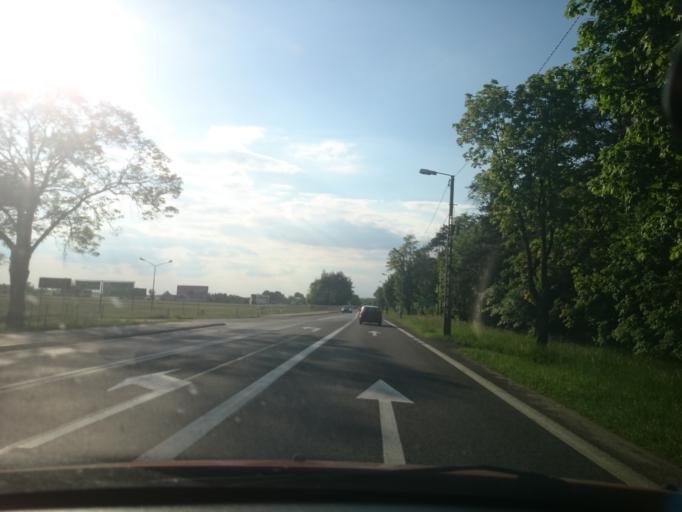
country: PL
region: Opole Voivodeship
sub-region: Powiat strzelecki
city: Izbicko
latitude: 50.5493
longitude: 18.2284
